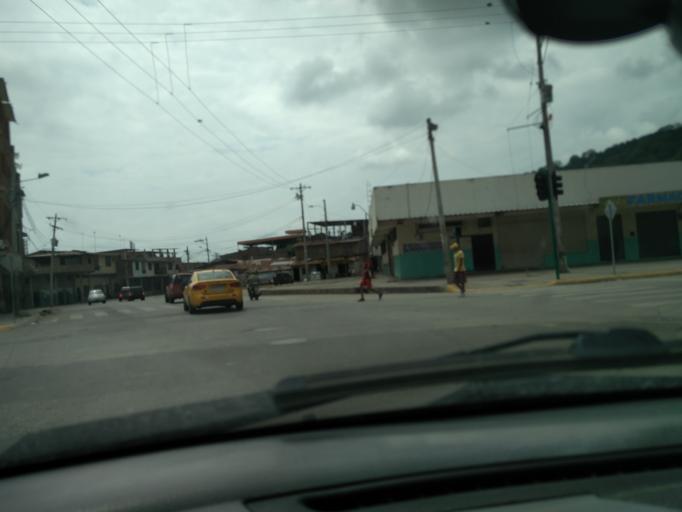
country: EC
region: Manabi
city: Portoviejo
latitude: -1.0512
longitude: -80.4502
